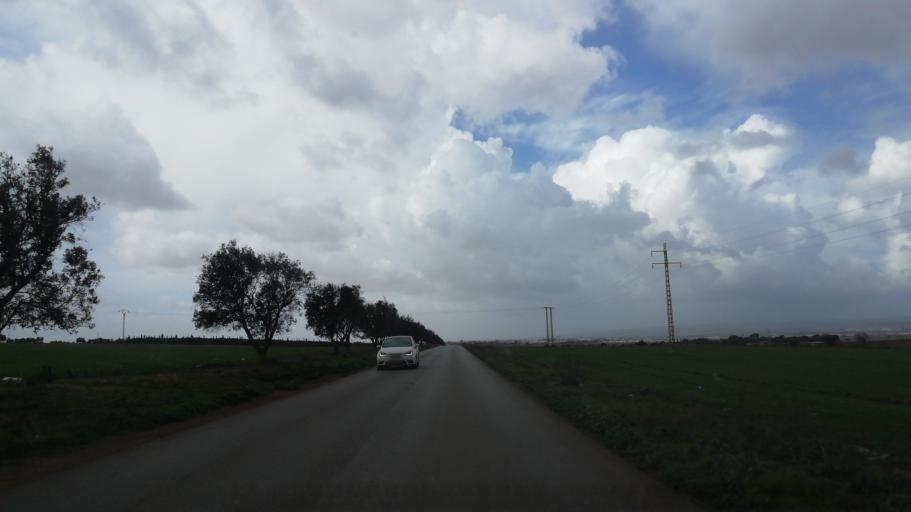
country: DZ
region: Oran
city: Sidi ech Chahmi
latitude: 35.6258
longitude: -0.5373
